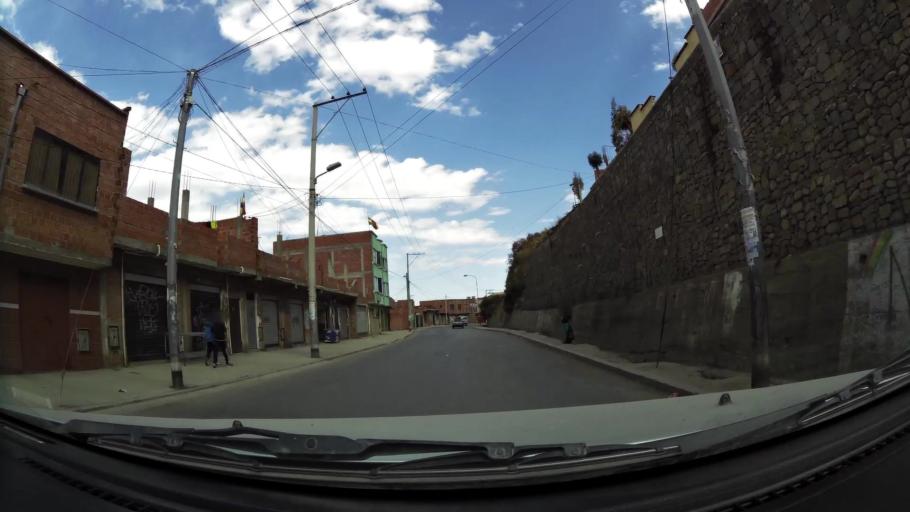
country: BO
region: La Paz
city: La Paz
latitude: -16.4670
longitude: -68.1194
